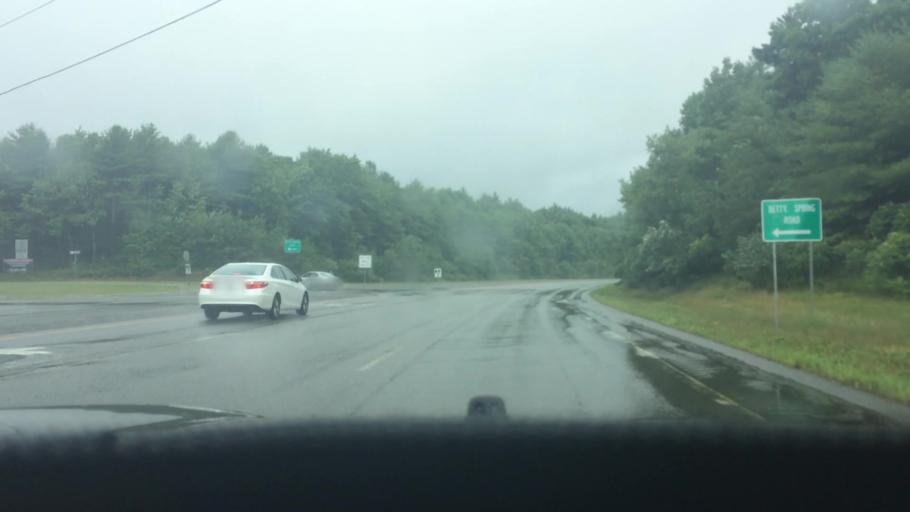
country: US
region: Massachusetts
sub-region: Worcester County
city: Westminster
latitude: 42.5653
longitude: -71.9439
